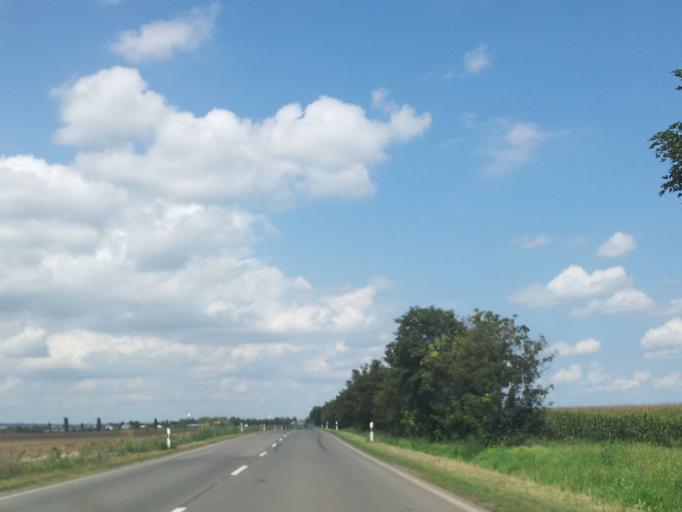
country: HU
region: Baranya
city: Mohacs
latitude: 45.9638
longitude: 18.6711
